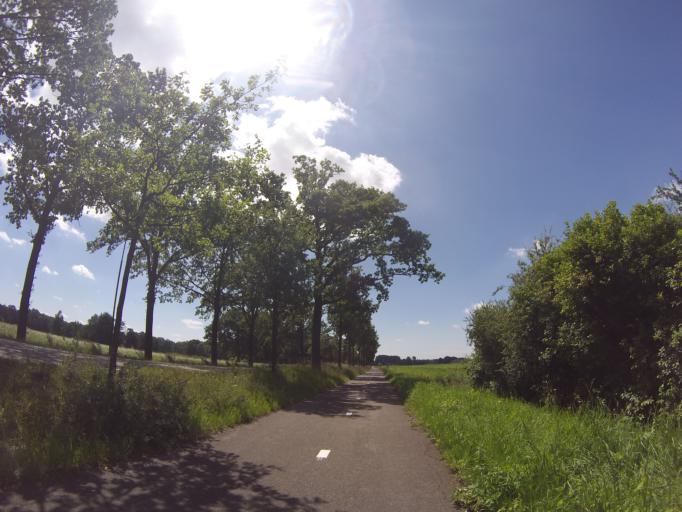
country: NL
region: Utrecht
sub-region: Stichtse Vecht
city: Spechtenkamp
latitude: 52.1303
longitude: 4.9847
